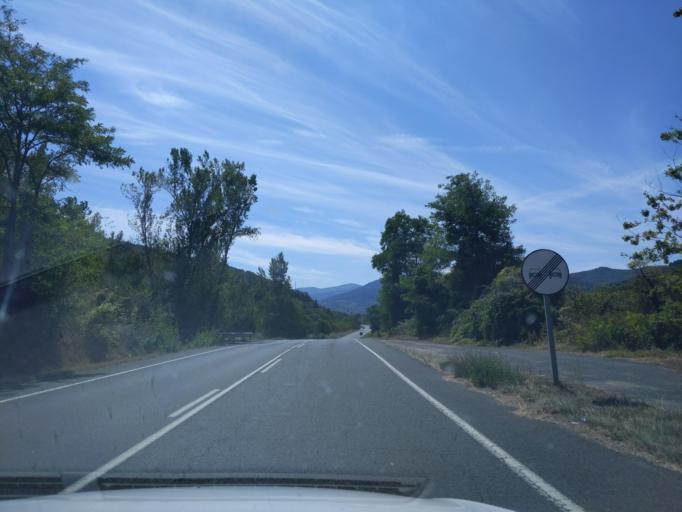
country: ES
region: La Rioja
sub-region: Provincia de La Rioja
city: Ojacastro
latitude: 42.3594
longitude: -2.9891
